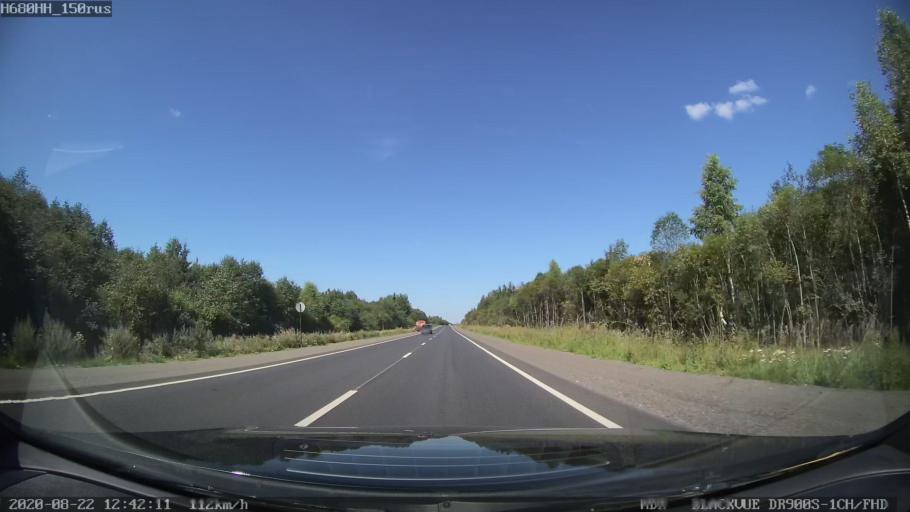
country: RU
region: Tverskaya
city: Rameshki
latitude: 57.3580
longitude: 36.0956
